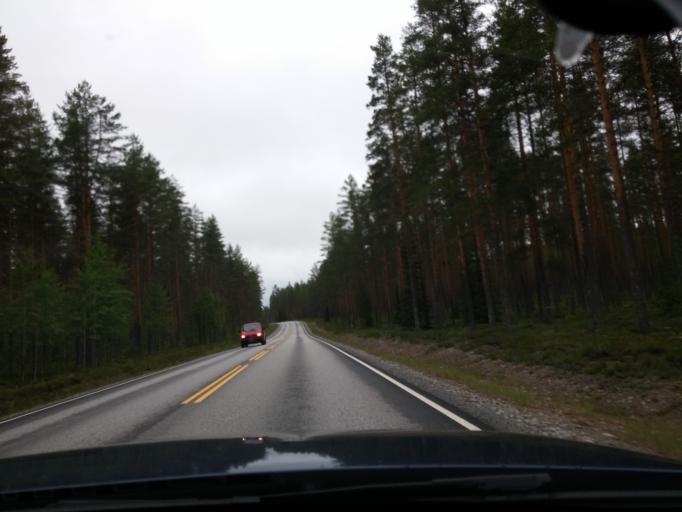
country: FI
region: Central Finland
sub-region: Keuruu
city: Multia
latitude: 62.5014
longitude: 24.6848
